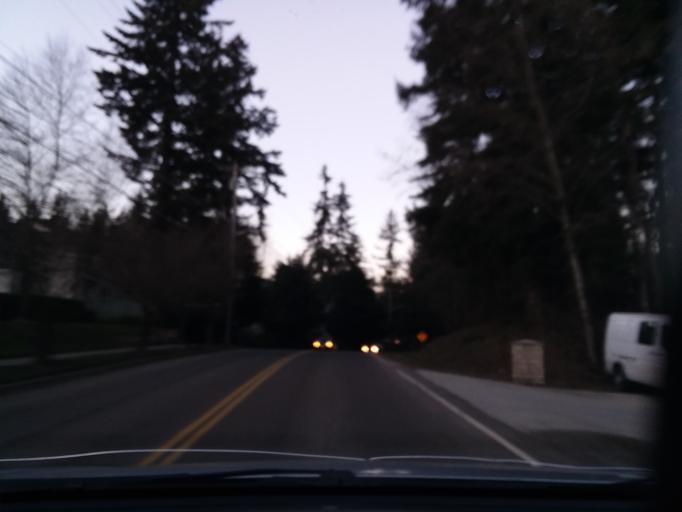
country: US
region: Washington
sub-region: Snohomish County
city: Martha Lake
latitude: 47.8829
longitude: -122.2560
